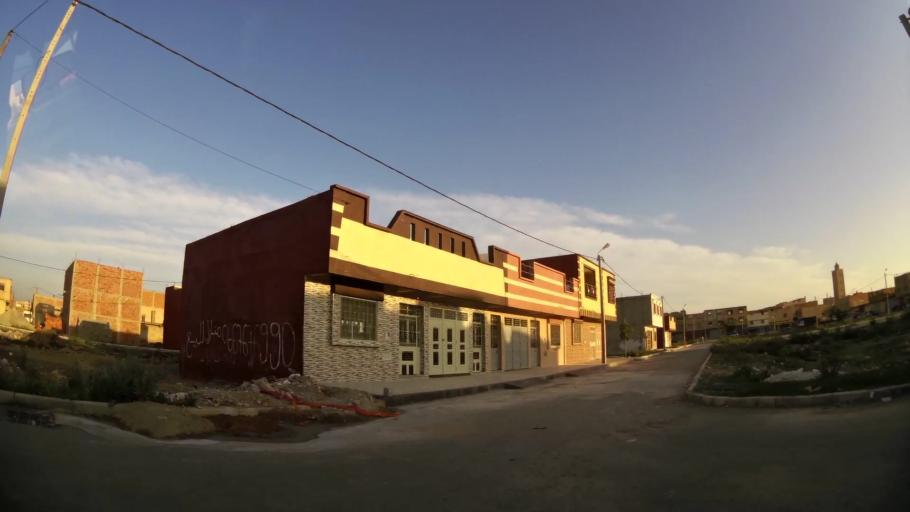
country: MA
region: Oriental
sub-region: Oujda-Angad
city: Oujda
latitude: 34.7127
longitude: -1.9075
